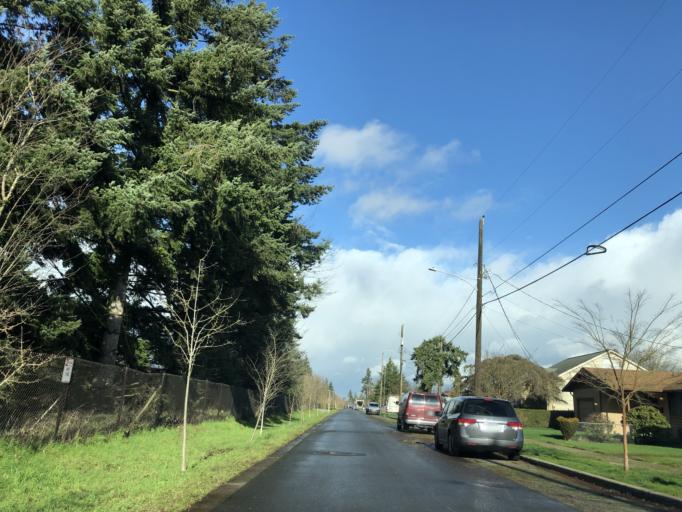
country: US
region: Washington
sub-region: Pierce County
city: Tacoma
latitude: 47.2376
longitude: -122.4629
